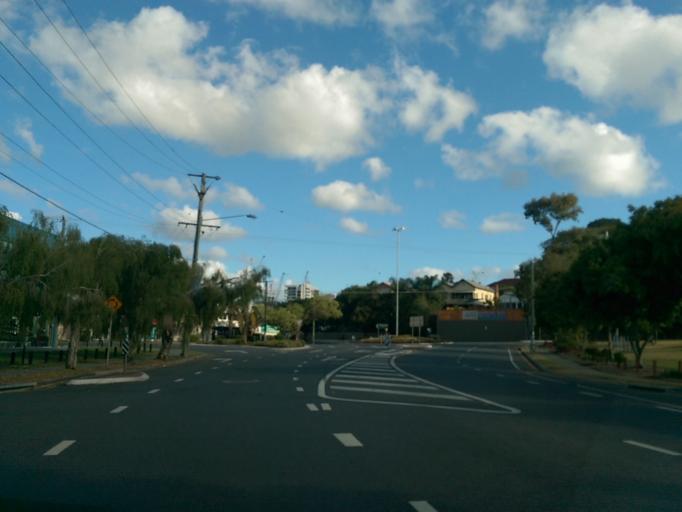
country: AU
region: Queensland
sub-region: Brisbane
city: Windsor
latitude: -27.4436
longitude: 153.0416
